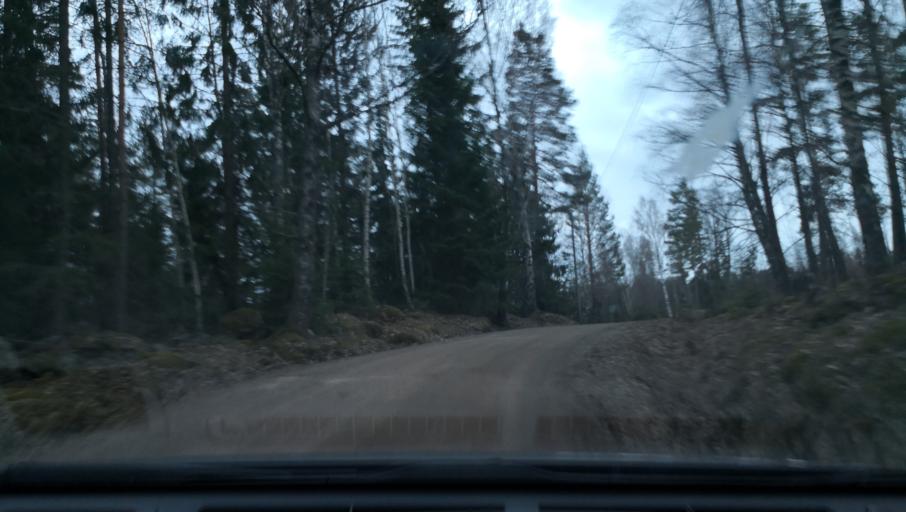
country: SE
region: OErebro
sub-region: Lindesbergs Kommun
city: Fellingsbro
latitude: 59.5757
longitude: 15.5663
